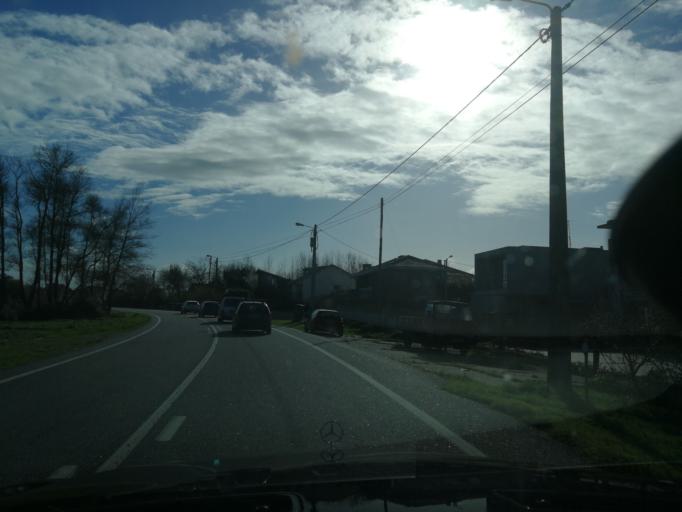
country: PT
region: Aveiro
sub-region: Estarreja
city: Pardilho
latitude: 40.8007
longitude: -8.6745
